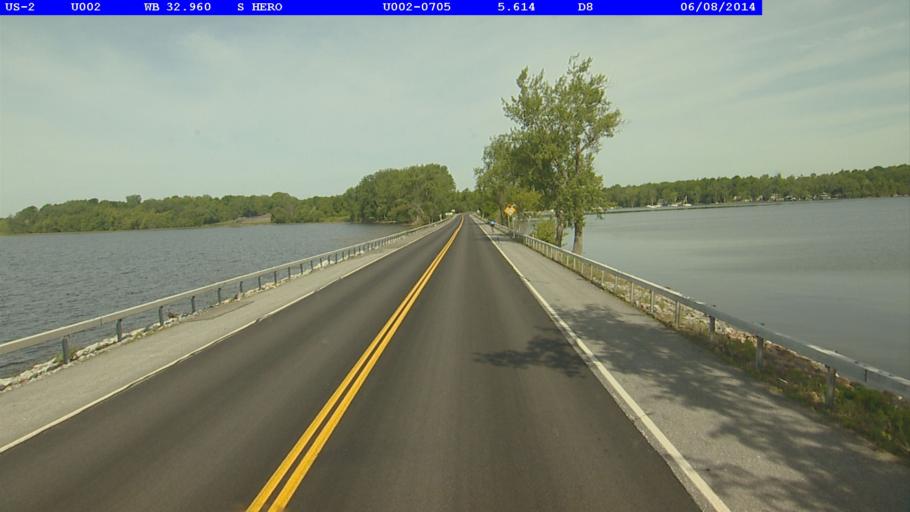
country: US
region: Vermont
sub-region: Chittenden County
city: Colchester
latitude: 44.6326
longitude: -73.2591
